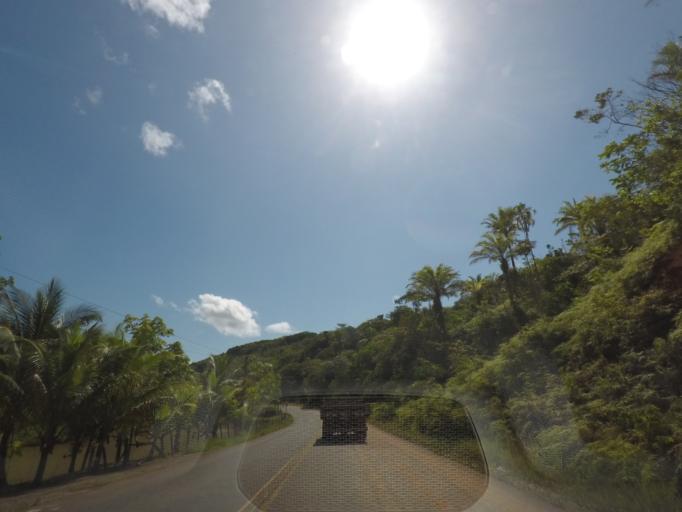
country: BR
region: Bahia
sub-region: Itubera
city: Itubera
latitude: -13.6972
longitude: -39.1340
